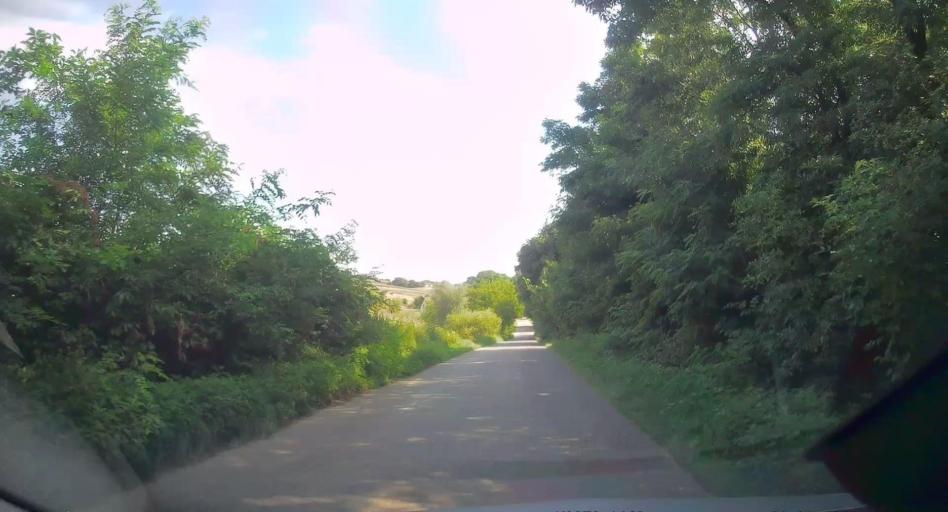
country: PL
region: Lesser Poland Voivodeship
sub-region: Powiat proszowicki
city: Nowe Brzesko
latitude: 50.1490
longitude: 20.4364
